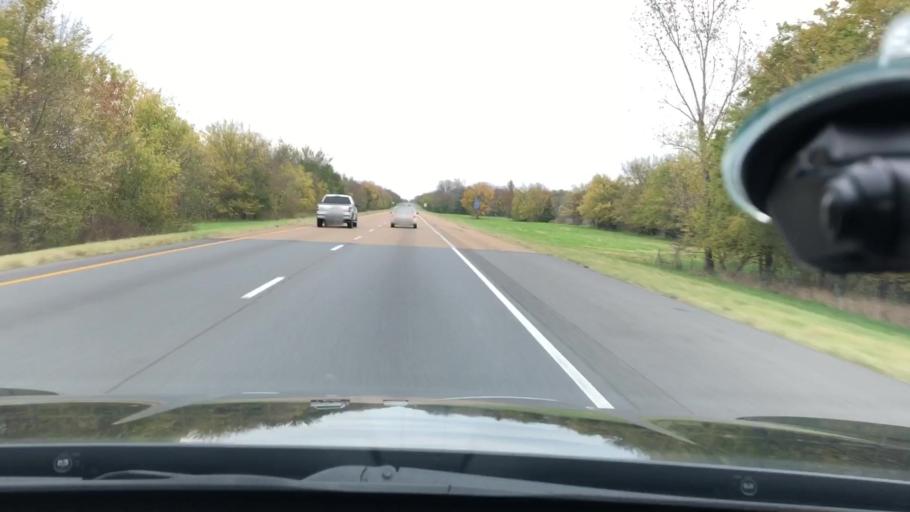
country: US
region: Arkansas
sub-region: Hempstead County
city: Hope
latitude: 33.7412
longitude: -93.5180
